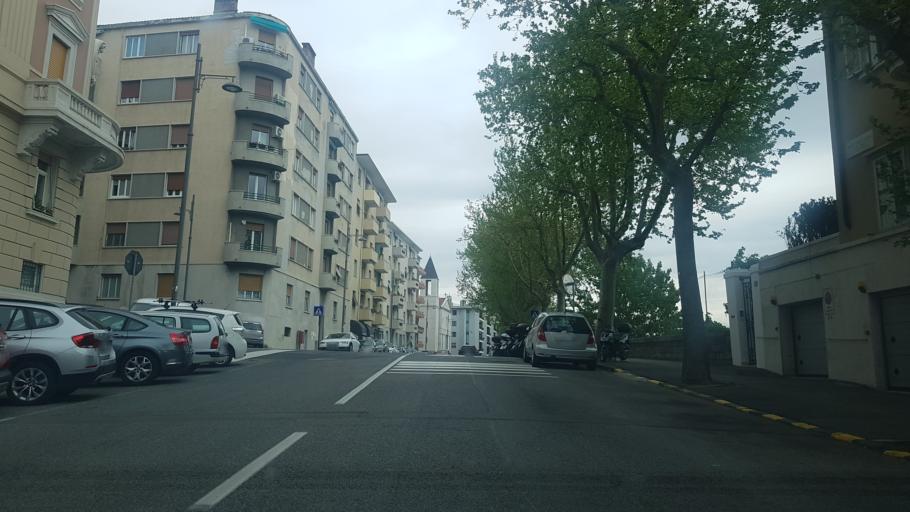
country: IT
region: Friuli Venezia Giulia
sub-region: Provincia di Trieste
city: Trieste
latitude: 45.6419
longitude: 13.7583
